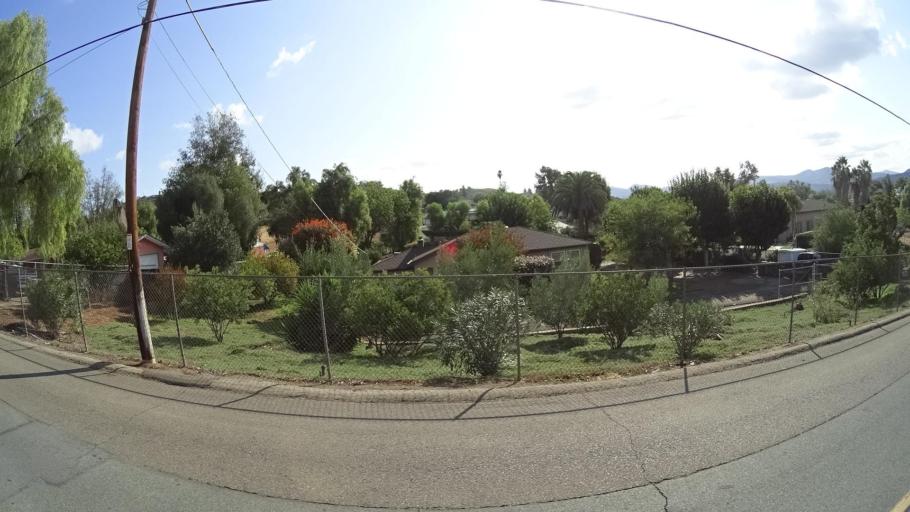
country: US
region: California
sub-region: San Diego County
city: Eucalyptus Hills
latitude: 32.8716
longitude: -116.9390
